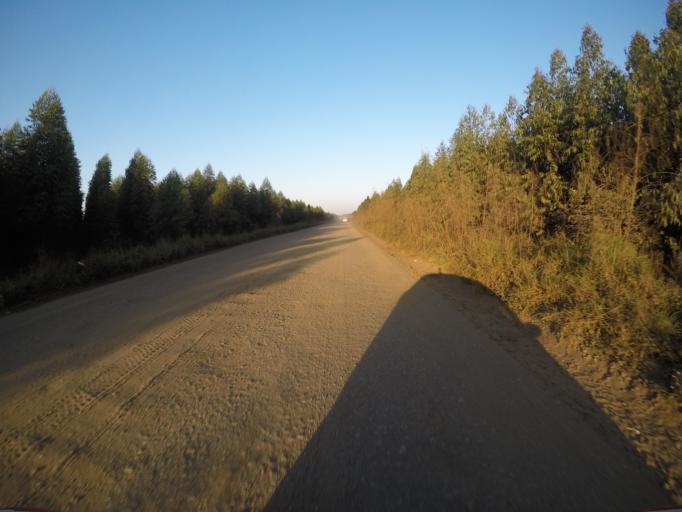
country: ZA
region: KwaZulu-Natal
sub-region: uThungulu District Municipality
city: KwaMbonambi
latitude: -28.6662
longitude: 32.0650
